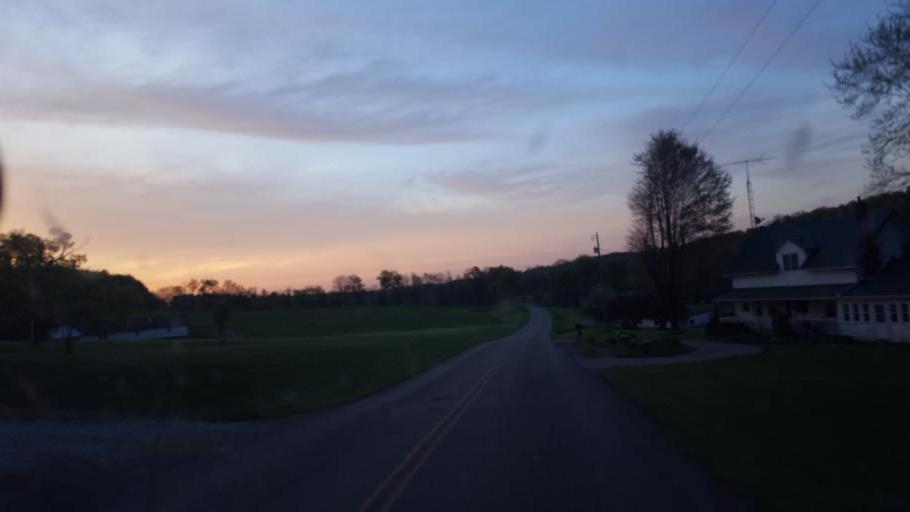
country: US
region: Ohio
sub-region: Knox County
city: Danville
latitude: 40.4676
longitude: -82.3216
